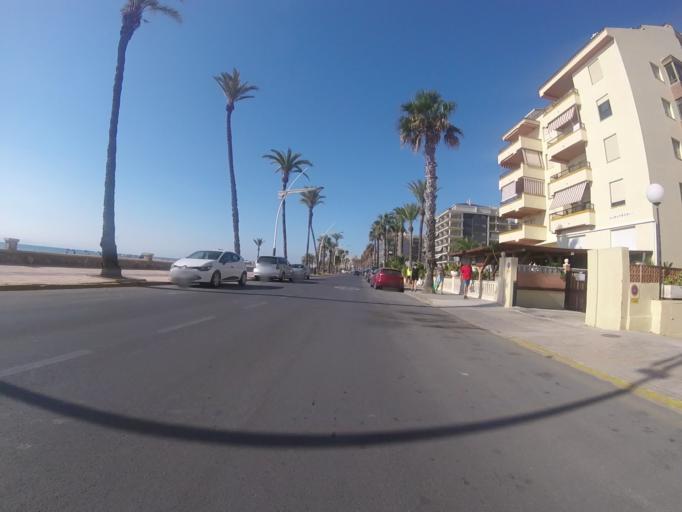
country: ES
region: Valencia
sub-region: Provincia de Castello
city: Peniscola
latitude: 40.3729
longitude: 0.4056
